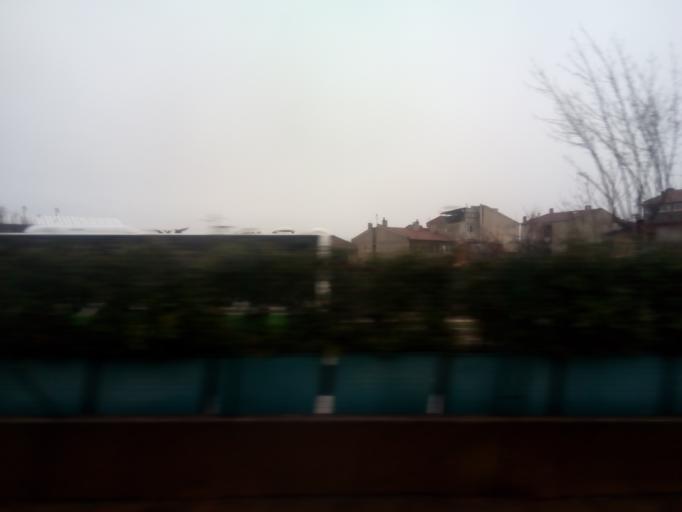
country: TR
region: Bursa
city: Yildirim
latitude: 40.2043
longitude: 29.0317
